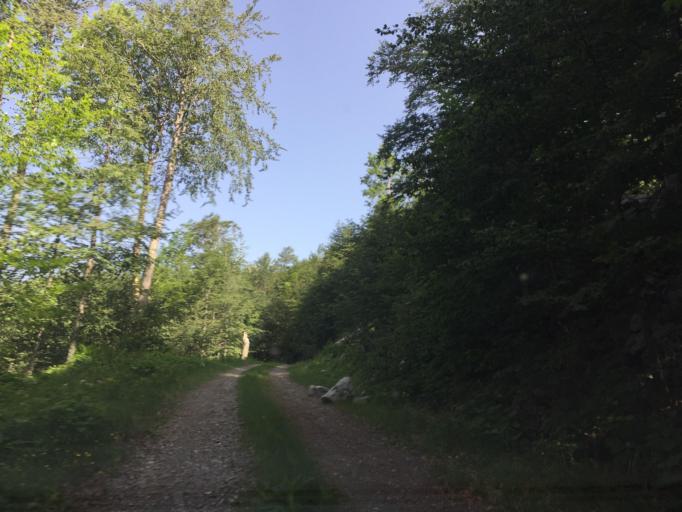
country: HR
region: Primorsko-Goranska
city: Podhum
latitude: 45.4206
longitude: 14.5873
